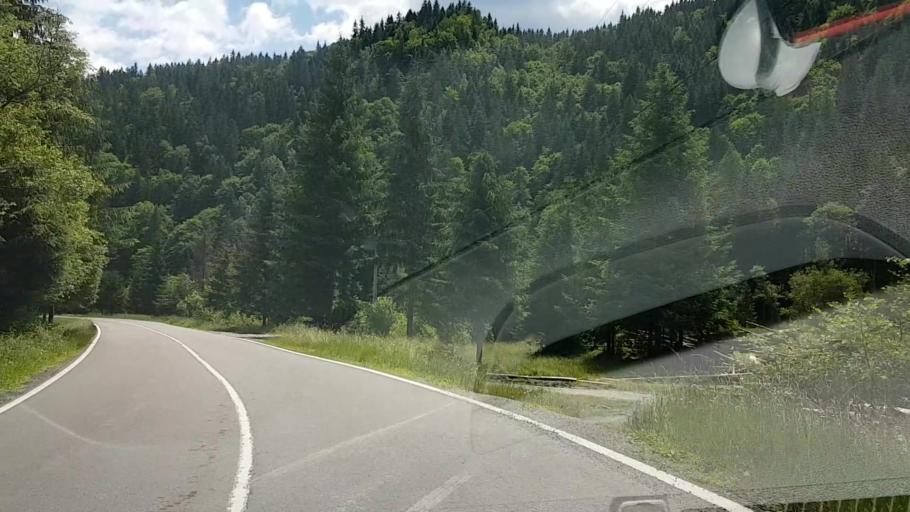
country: RO
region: Suceava
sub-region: Comuna Crucea
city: Crucea
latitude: 47.3815
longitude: 25.5751
